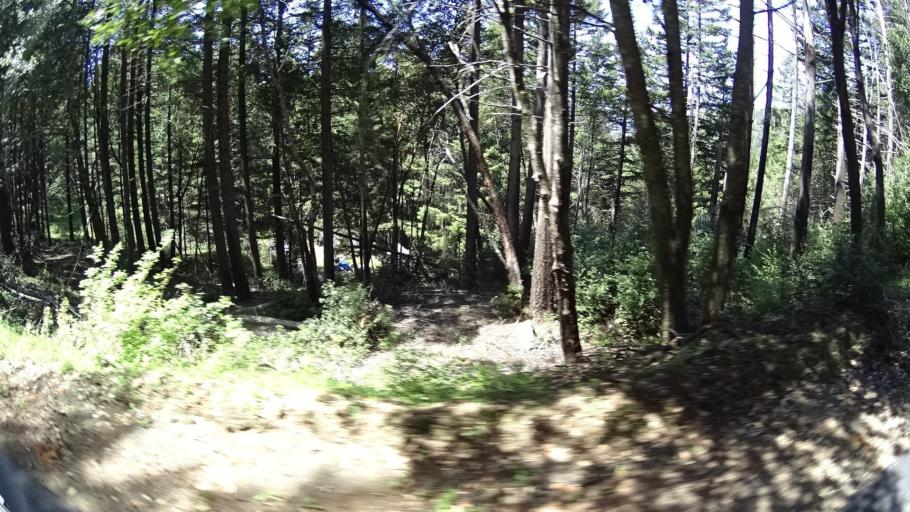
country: US
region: California
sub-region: Humboldt County
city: Rio Dell
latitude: 40.2647
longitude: -124.0908
